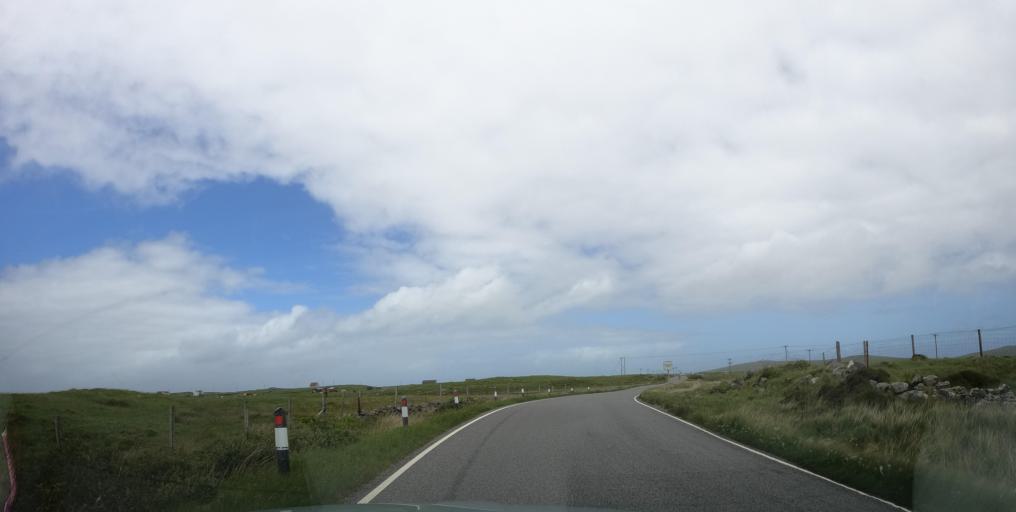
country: GB
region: Scotland
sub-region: Eilean Siar
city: Isle of South Uist
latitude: 57.3076
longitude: -7.3710
